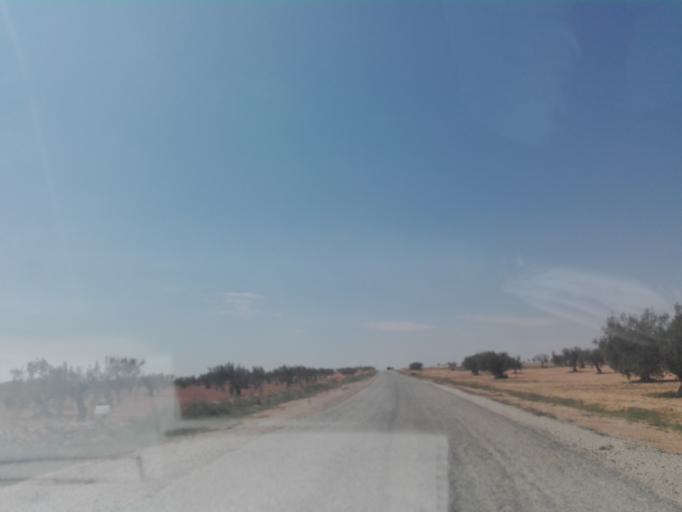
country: TN
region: Safaqis
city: Bi'r `Ali Bin Khalifah
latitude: 34.6444
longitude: 10.4095
